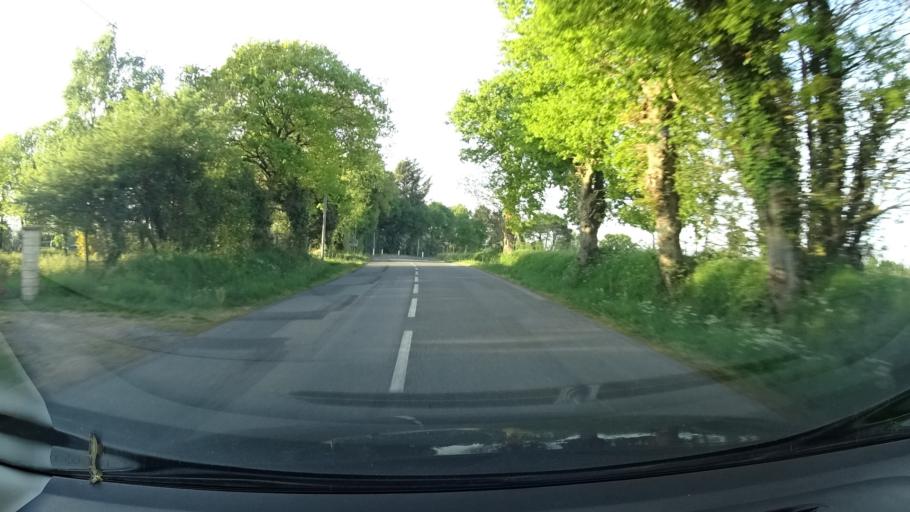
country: FR
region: Brittany
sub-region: Departement du Morbihan
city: Caden
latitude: 47.5926
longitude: -2.2926
